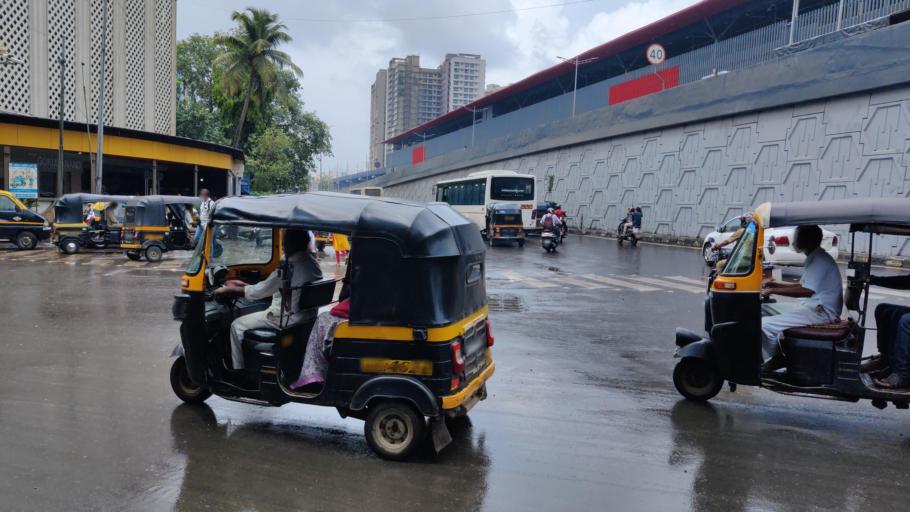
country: IN
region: Maharashtra
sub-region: Mumbai Suburban
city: Borivli
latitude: 19.2443
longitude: 72.8648
